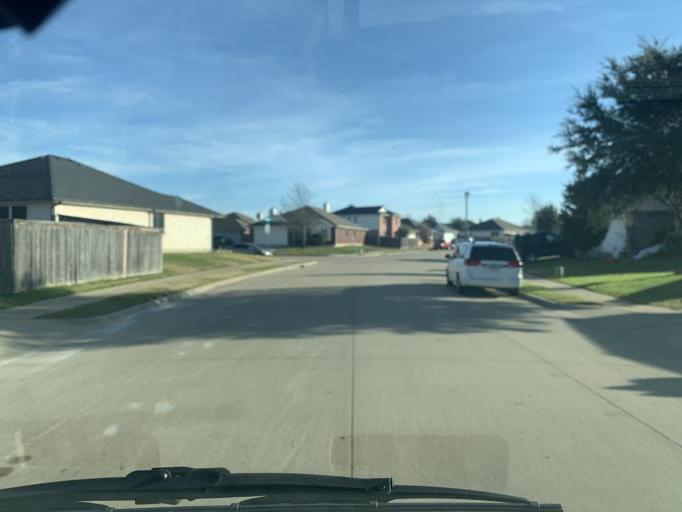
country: US
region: Texas
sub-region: Dallas County
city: Duncanville
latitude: 32.6556
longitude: -96.9752
